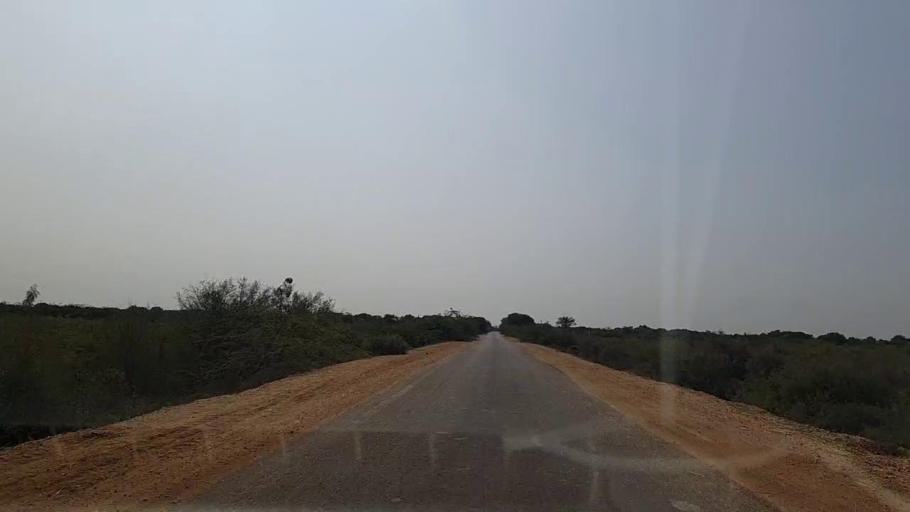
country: PK
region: Sindh
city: Chuhar Jamali
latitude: 24.2708
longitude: 67.9127
